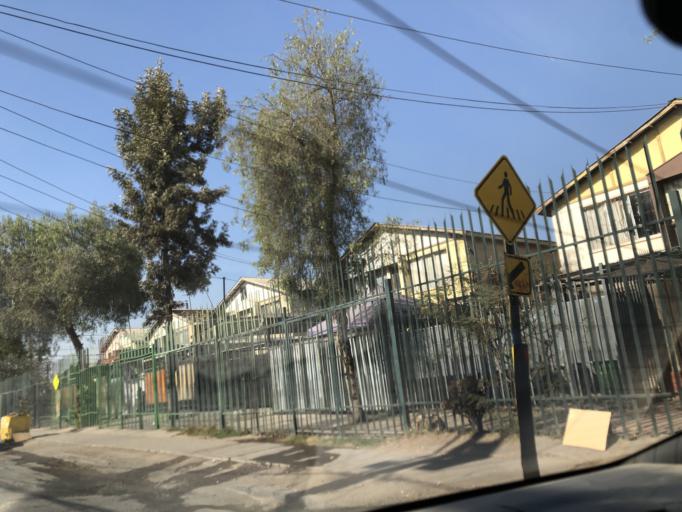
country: CL
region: Santiago Metropolitan
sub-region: Provincia de Cordillera
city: Puente Alto
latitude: -33.5938
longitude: -70.6029
